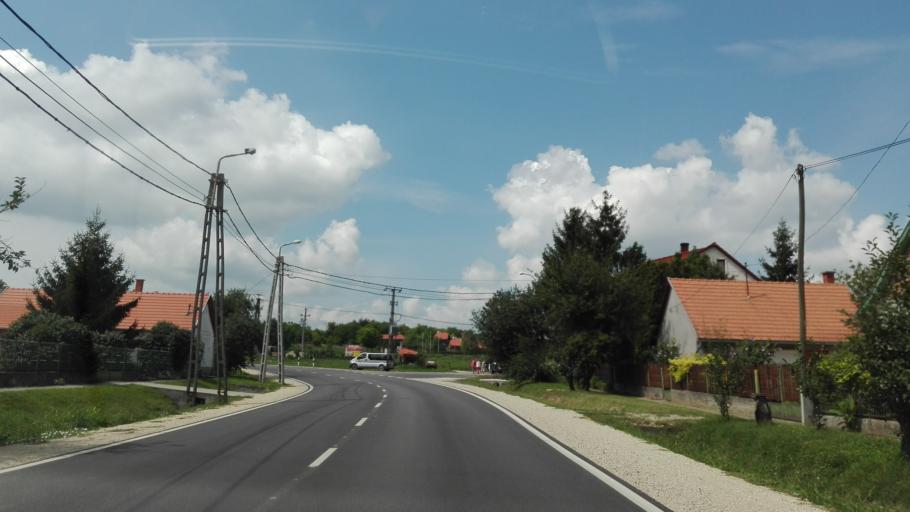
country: HU
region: Tolna
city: Simontornya
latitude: 46.7598
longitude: 18.5409
